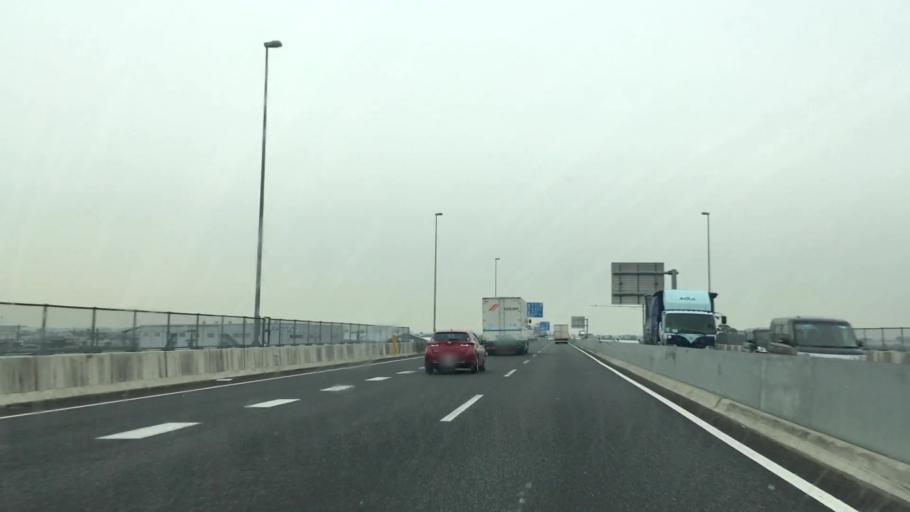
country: JP
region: Aichi
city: Anjo
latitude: 34.9568
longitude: 137.0373
